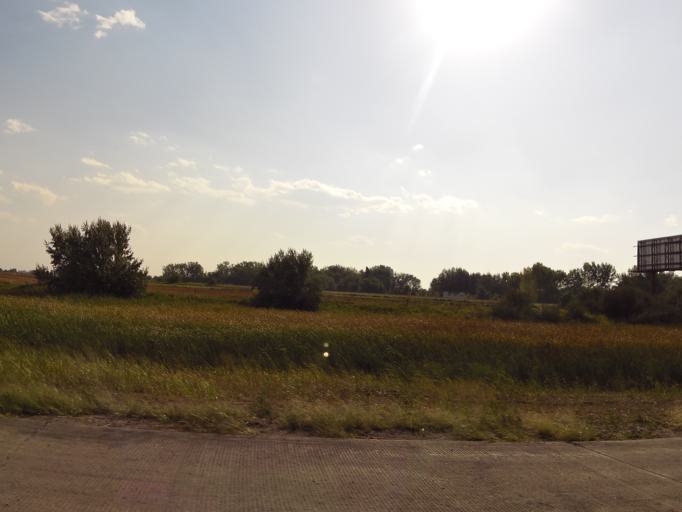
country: US
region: North Dakota
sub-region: Grand Forks County
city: Grand Forks
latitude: 48.0023
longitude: -97.1016
